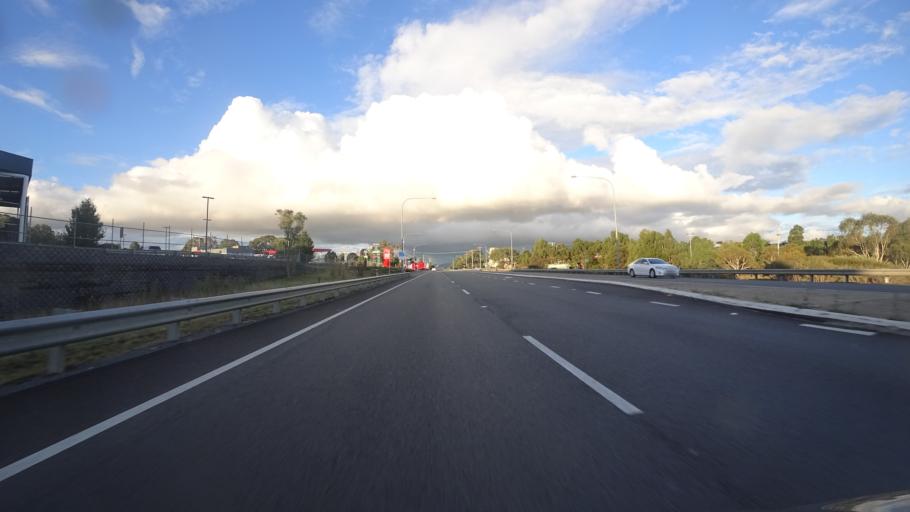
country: AU
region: New South Wales
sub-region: Goulburn Mulwaree
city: Goulburn
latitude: -34.7736
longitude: 149.6891
